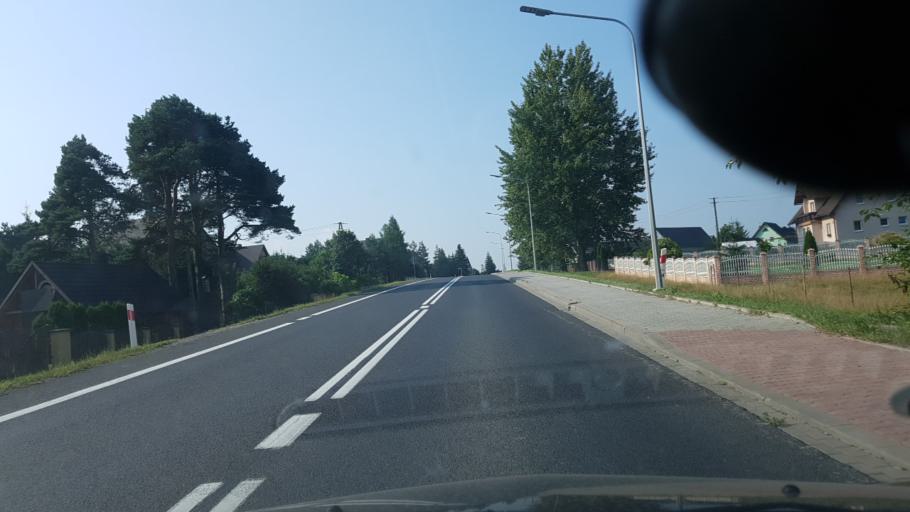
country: PL
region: Lesser Poland Voivodeship
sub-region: Powiat nowotarski
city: Jablonka
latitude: 49.4601
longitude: 19.6905
